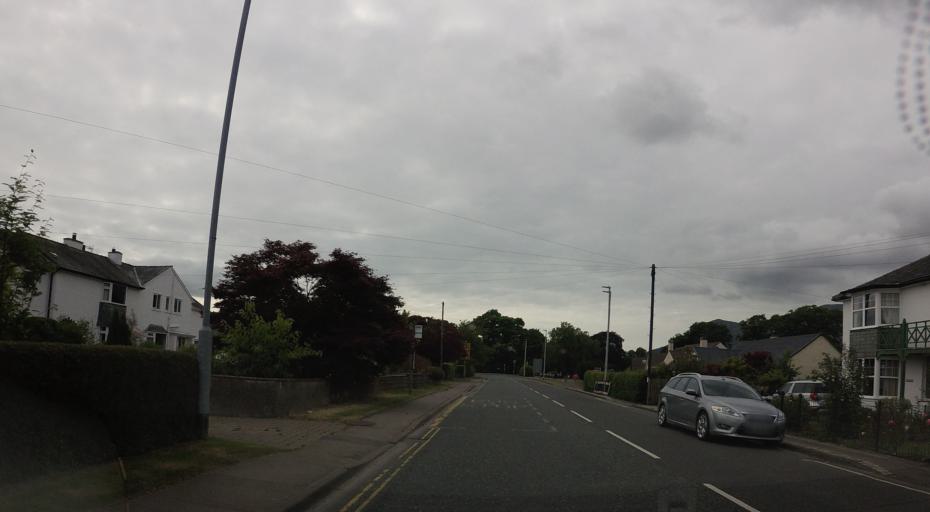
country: GB
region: England
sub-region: Cumbria
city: Keswick
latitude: 54.6057
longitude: -3.1468
